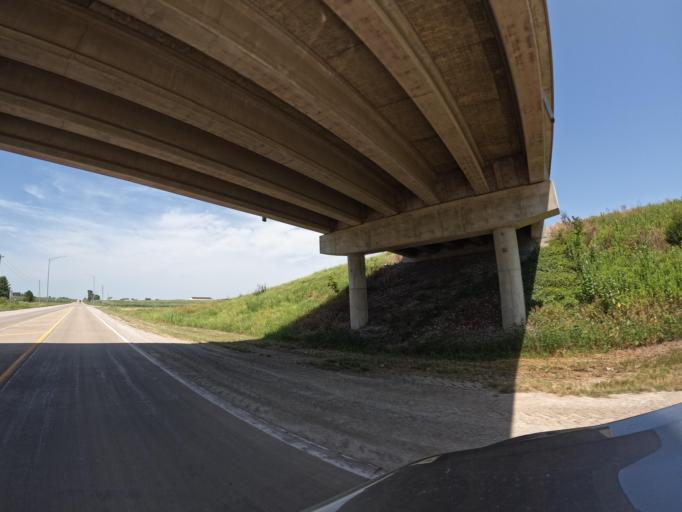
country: US
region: Iowa
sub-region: Henry County
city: Mount Pleasant
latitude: 40.9847
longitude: -91.6123
